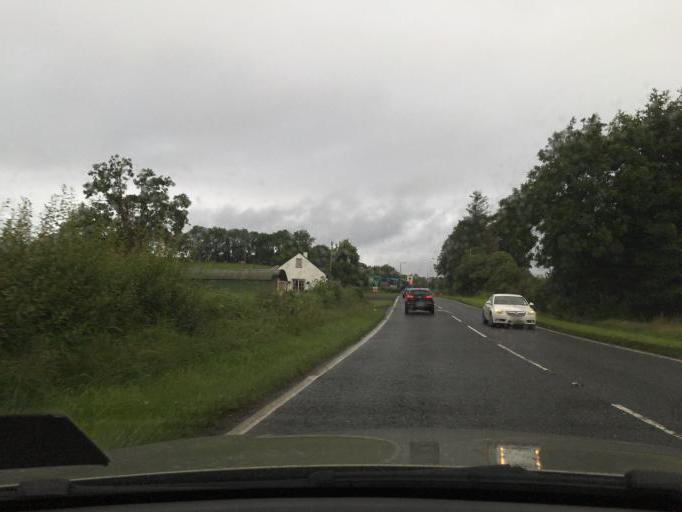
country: GB
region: Northern Ireland
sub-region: Fermanagh District
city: Enniskillen
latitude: 54.3839
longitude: -7.6375
